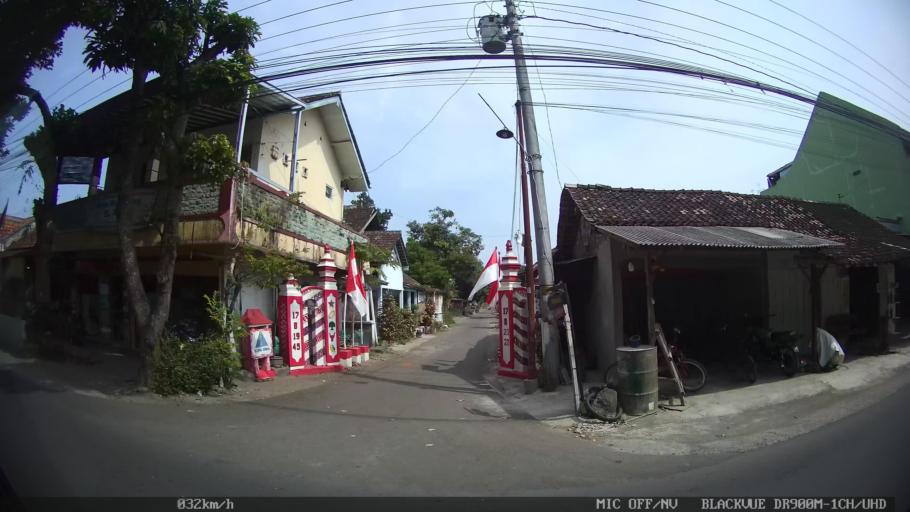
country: ID
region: Daerah Istimewa Yogyakarta
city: Depok
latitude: -7.8039
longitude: 110.4338
